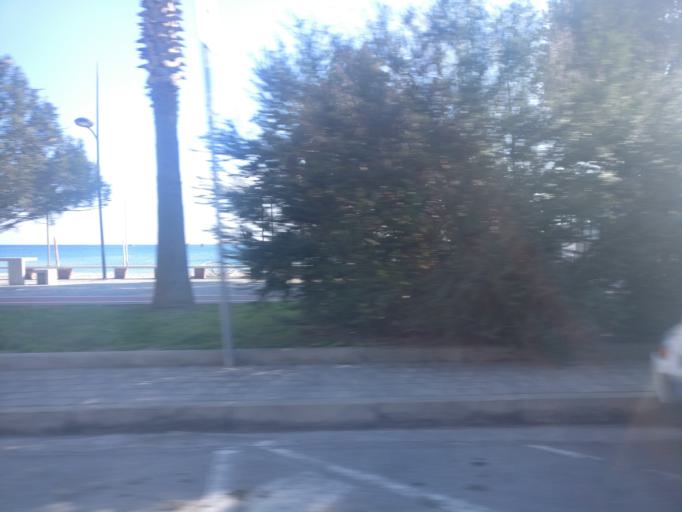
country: IT
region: Liguria
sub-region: Provincia di Savona
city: Vado Ligure
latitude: 44.2747
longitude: 8.4398
